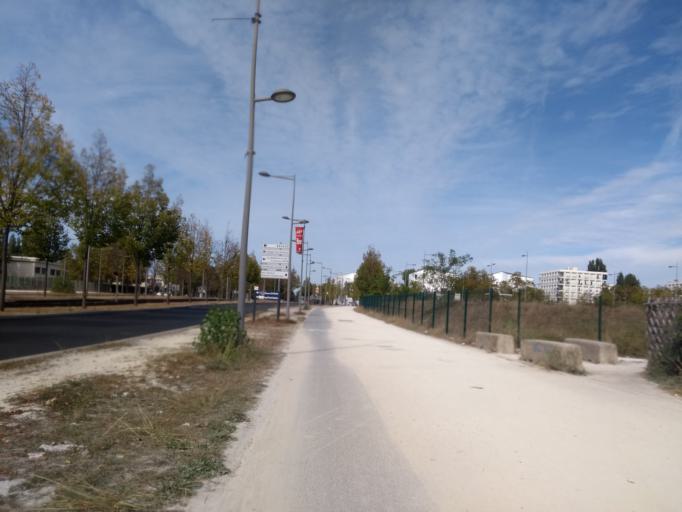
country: FR
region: Aquitaine
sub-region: Departement de la Gironde
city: Le Bouscat
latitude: 44.8724
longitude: -0.5762
